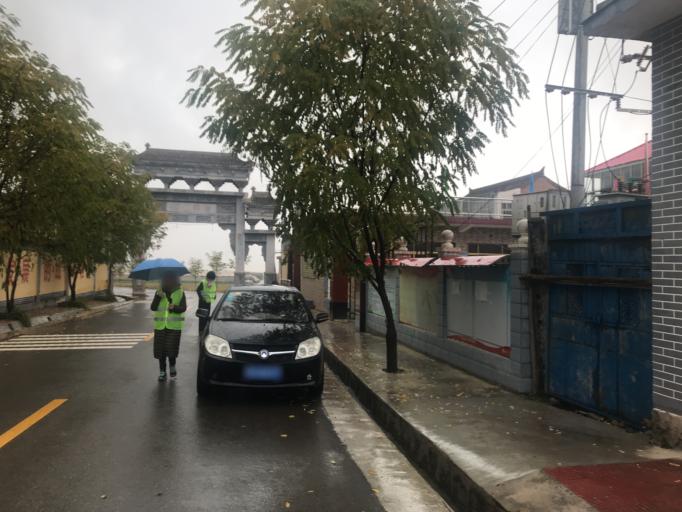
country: CN
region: Gansu Sheng
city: Maji
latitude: 35.3913
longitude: 103.0647
